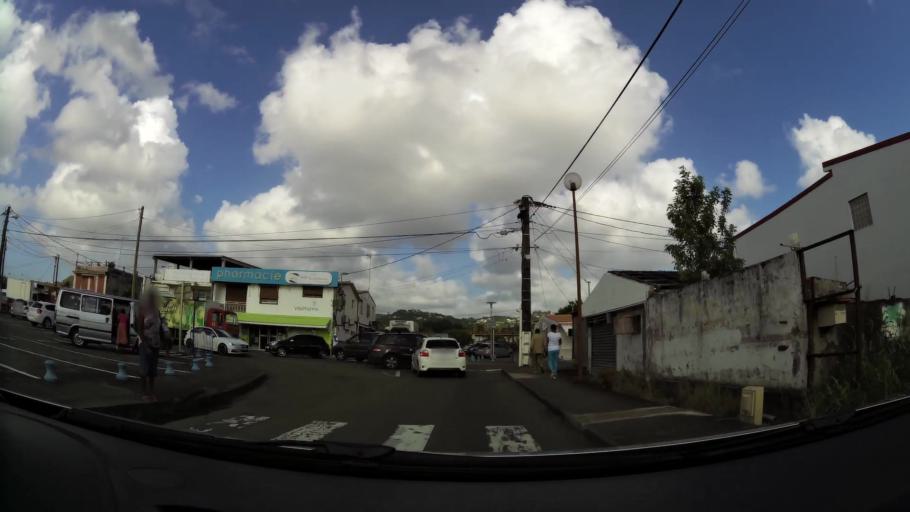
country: MQ
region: Martinique
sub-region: Martinique
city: Le Robert
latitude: 14.6759
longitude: -60.9406
